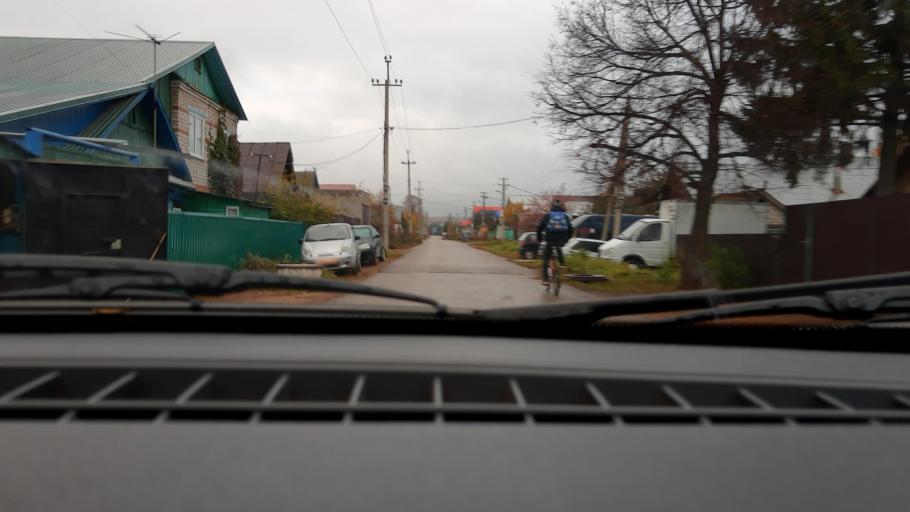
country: RU
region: Bashkortostan
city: Mikhaylovka
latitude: 54.7890
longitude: 55.8880
